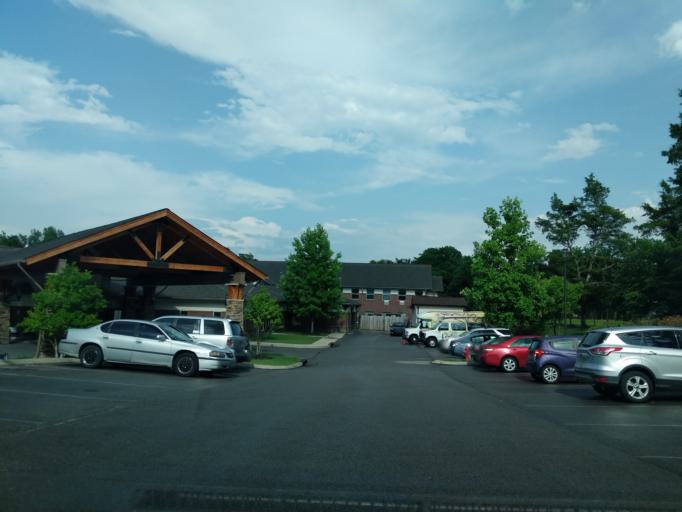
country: US
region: Tennessee
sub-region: Cheatham County
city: Pegram
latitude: 36.0419
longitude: -86.9569
